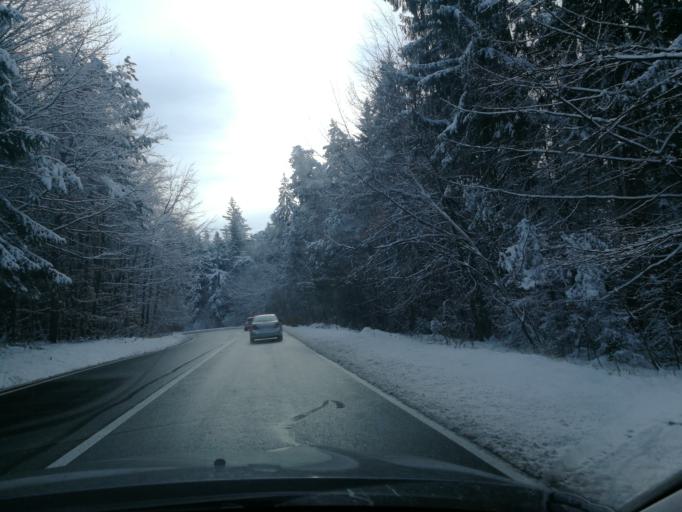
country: RO
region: Brasov
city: Brasov
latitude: 45.6281
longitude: 25.5568
